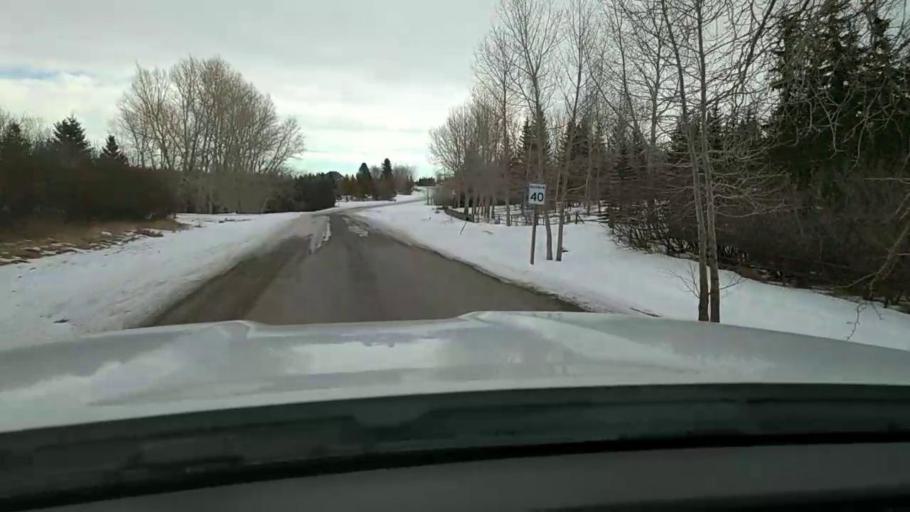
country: CA
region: Alberta
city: Cochrane
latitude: 51.2009
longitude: -114.2803
